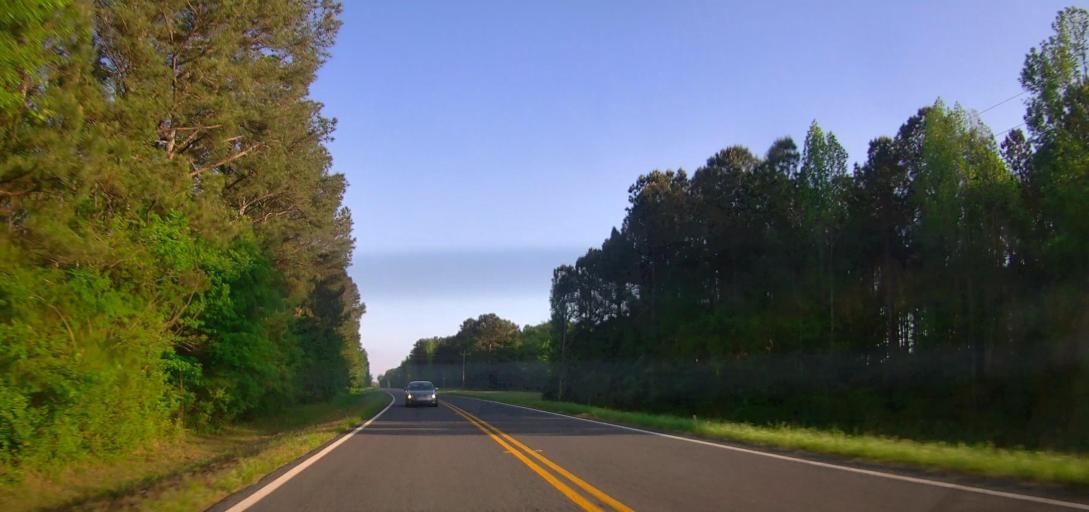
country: US
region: Georgia
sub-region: Walton County
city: Social Circle
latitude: 33.4892
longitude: -83.6496
